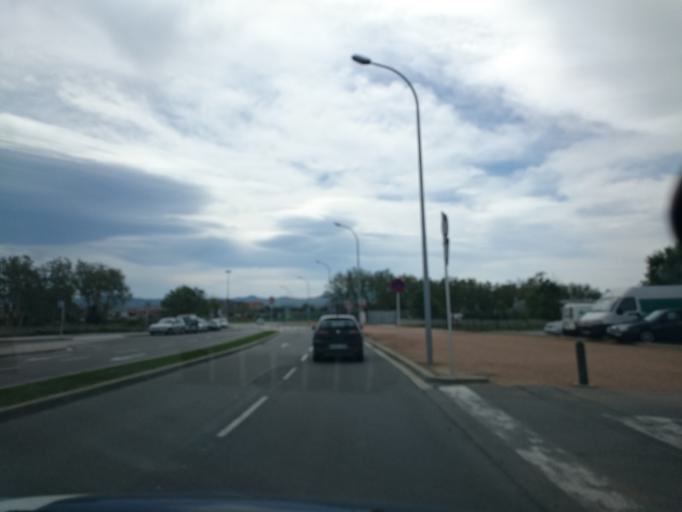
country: ES
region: Catalonia
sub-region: Provincia de Barcelona
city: Vic
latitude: 41.9190
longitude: 2.2503
